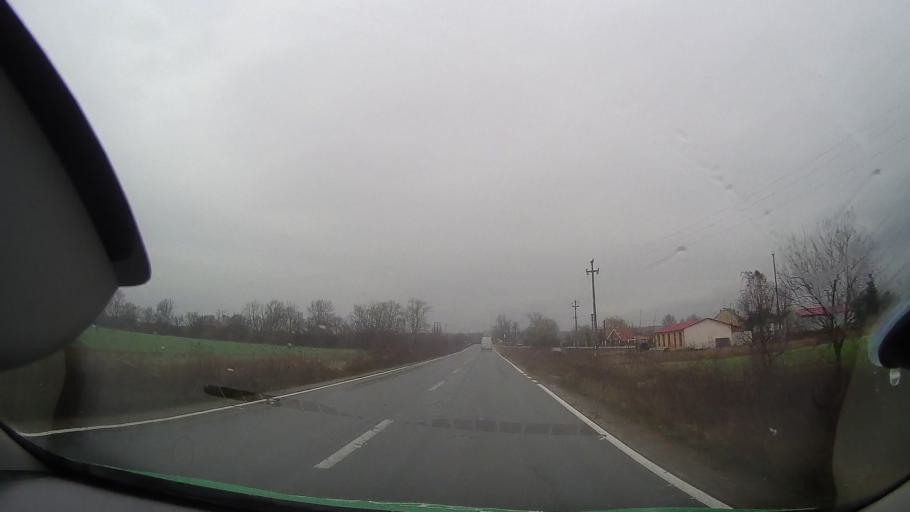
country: RO
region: Bihor
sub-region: Comuna Tinca
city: Tinca
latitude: 46.7662
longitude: 21.9334
